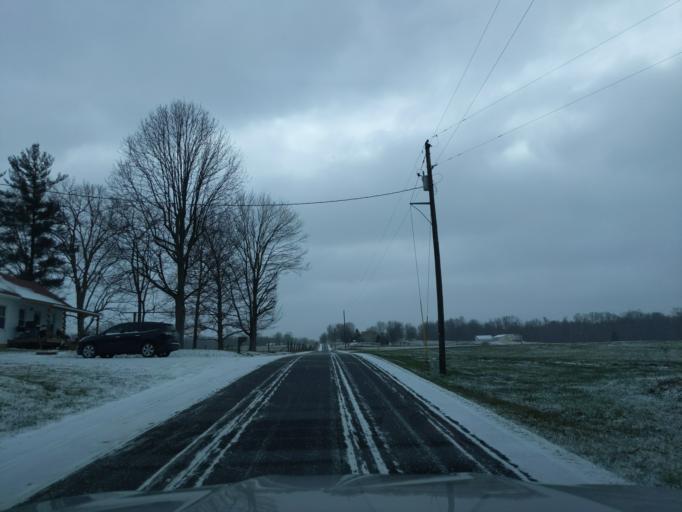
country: US
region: Indiana
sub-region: Decatur County
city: Westport
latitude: 39.2239
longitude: -85.5175
